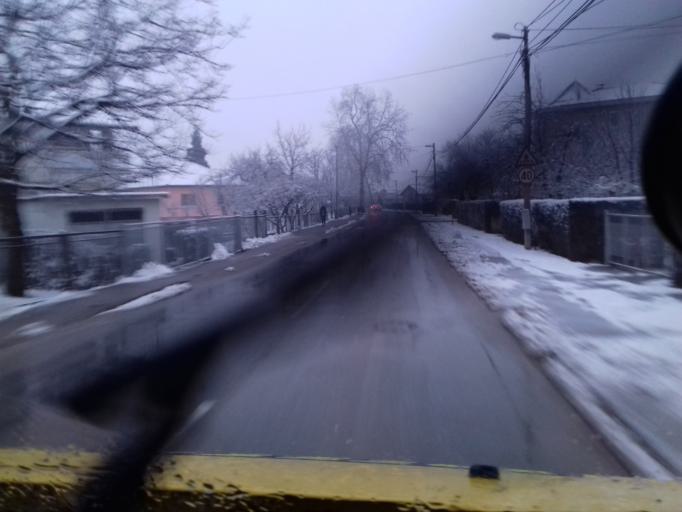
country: BA
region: Federation of Bosnia and Herzegovina
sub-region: Kanton Sarajevo
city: Sarajevo
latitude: 43.8189
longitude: 18.3263
